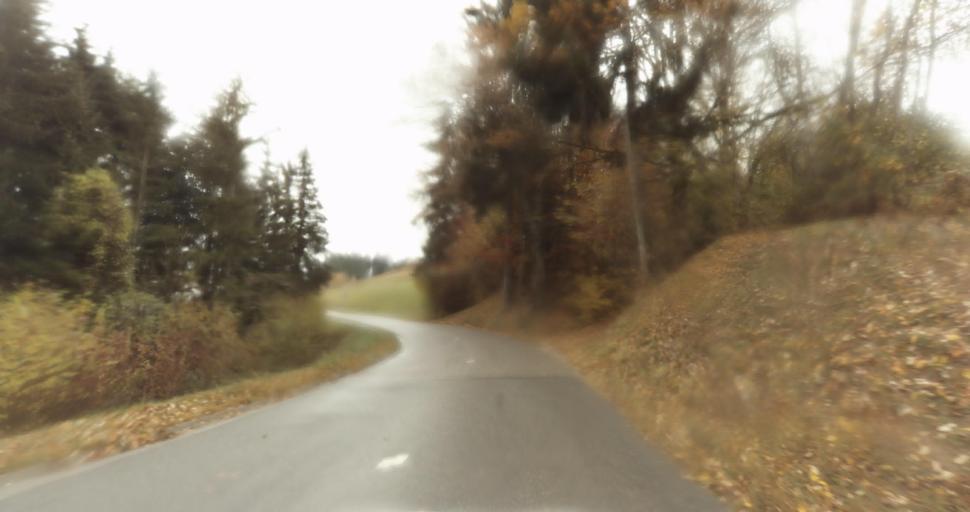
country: FR
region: Rhone-Alpes
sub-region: Departement de la Haute-Savoie
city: Thorens-Glieres
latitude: 46.0038
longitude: 6.2417
